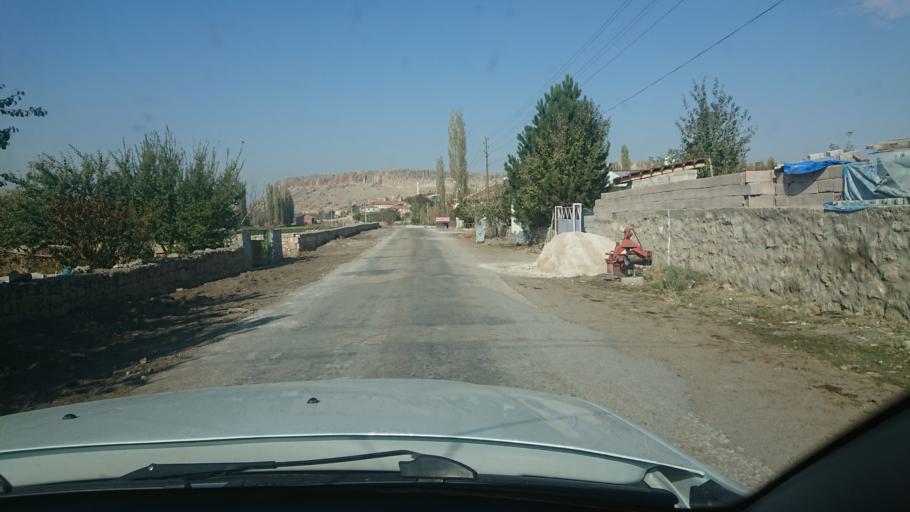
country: TR
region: Aksaray
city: Gulagac
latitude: 38.3507
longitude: 34.2348
